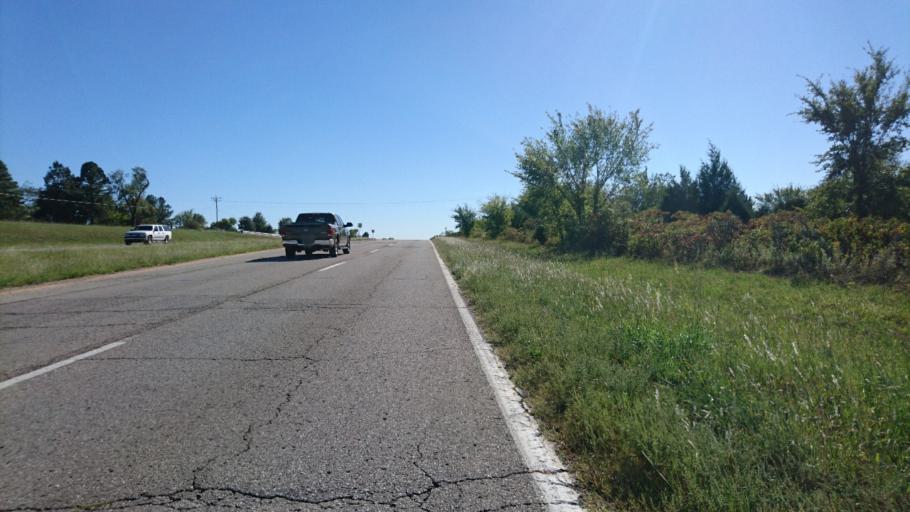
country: US
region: Oklahoma
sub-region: Rogers County
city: Bushyhead
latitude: 36.4167
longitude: -95.5360
